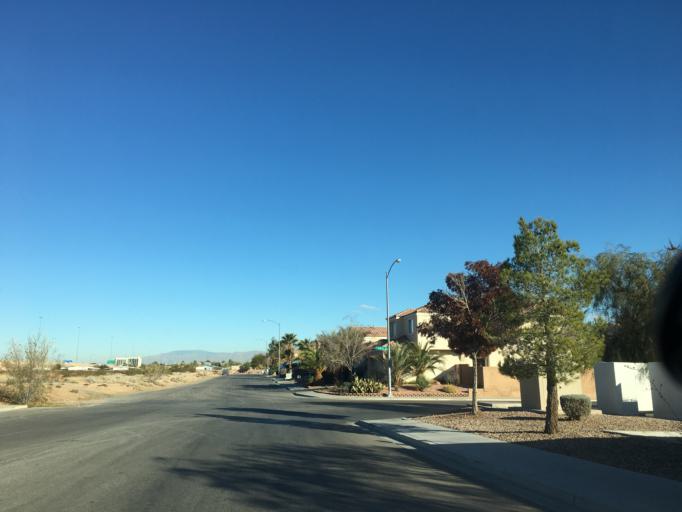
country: US
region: Nevada
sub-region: Clark County
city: Enterprise
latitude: 36.0151
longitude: -115.1788
